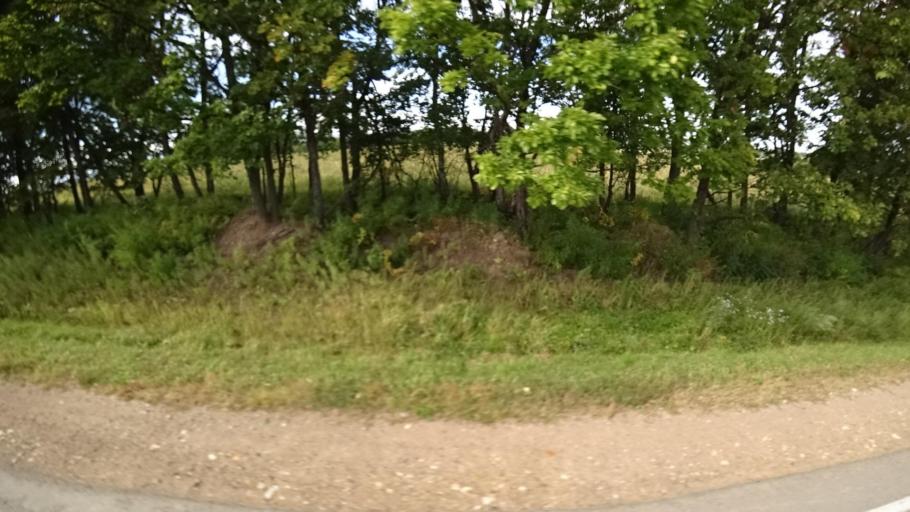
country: RU
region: Primorskiy
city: Dostoyevka
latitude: 44.3188
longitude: 133.4703
